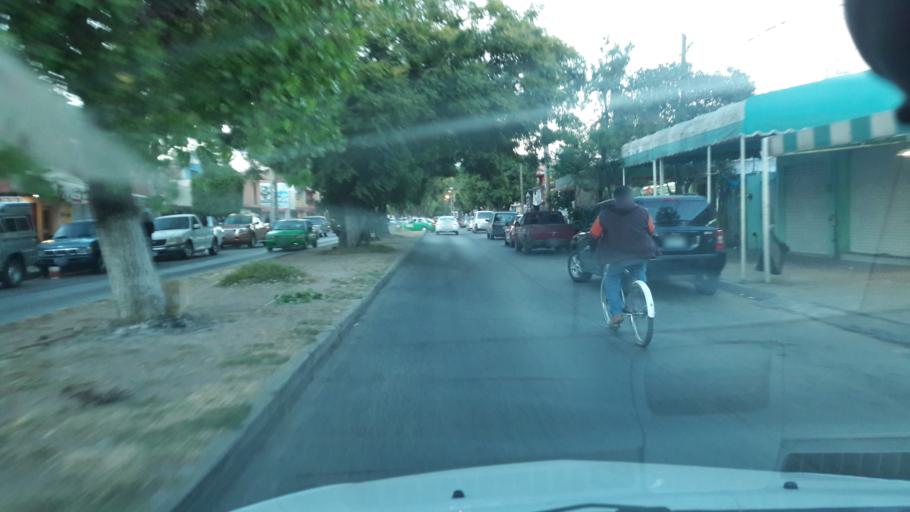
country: MX
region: Guanajuato
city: Leon
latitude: 21.1651
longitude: -101.6690
